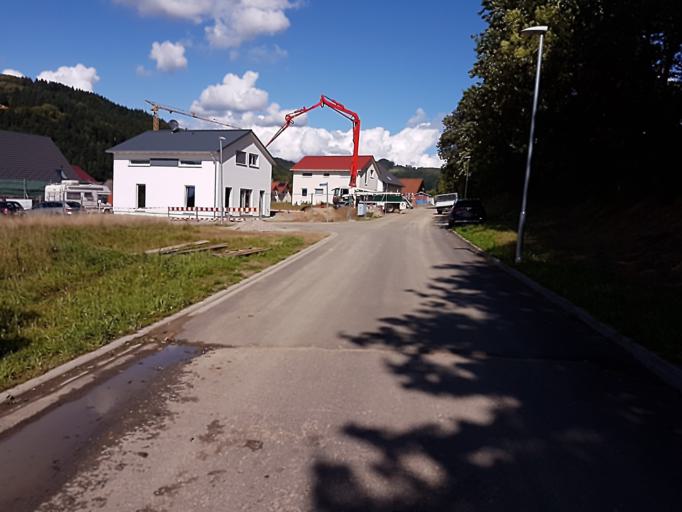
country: DE
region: Baden-Wuerttemberg
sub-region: Freiburg Region
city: Gutach im Breisgau
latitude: 48.1423
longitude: 8.0263
